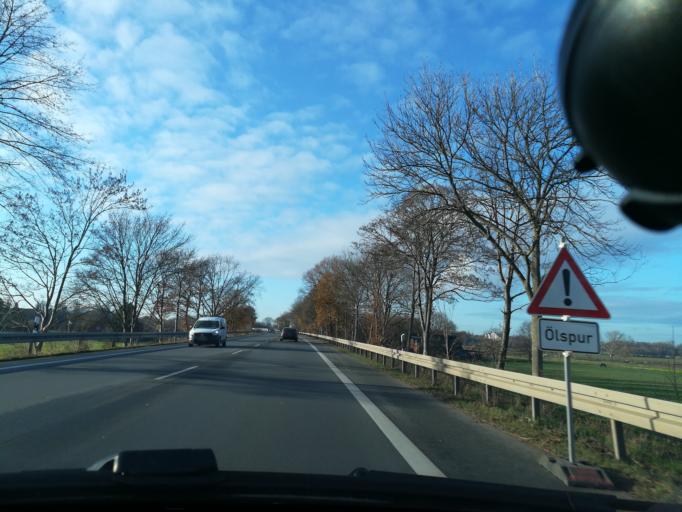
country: DE
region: North Rhine-Westphalia
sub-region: Regierungsbezirk Detmold
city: Petershagen
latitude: 52.3805
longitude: 8.9809
